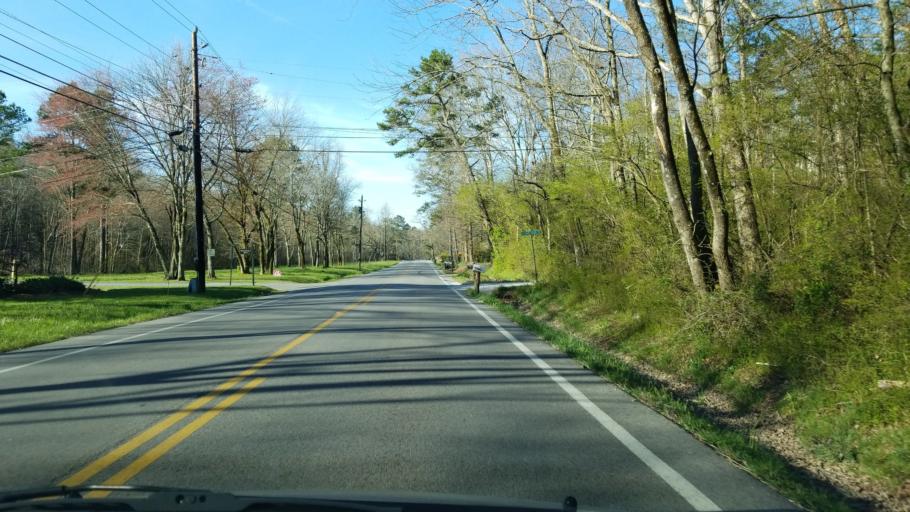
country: US
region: Tennessee
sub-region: Hamilton County
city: East Brainerd
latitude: 35.0126
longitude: -85.1143
